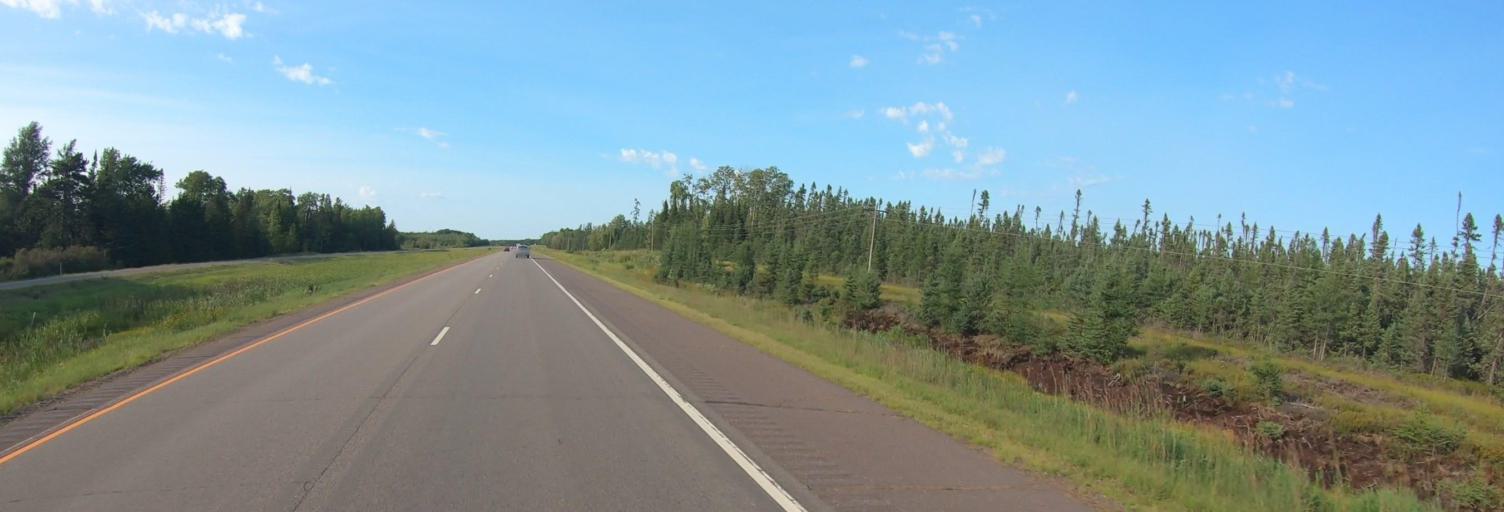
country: US
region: Minnesota
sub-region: Saint Louis County
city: Eveleth
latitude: 47.1149
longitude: -92.4718
